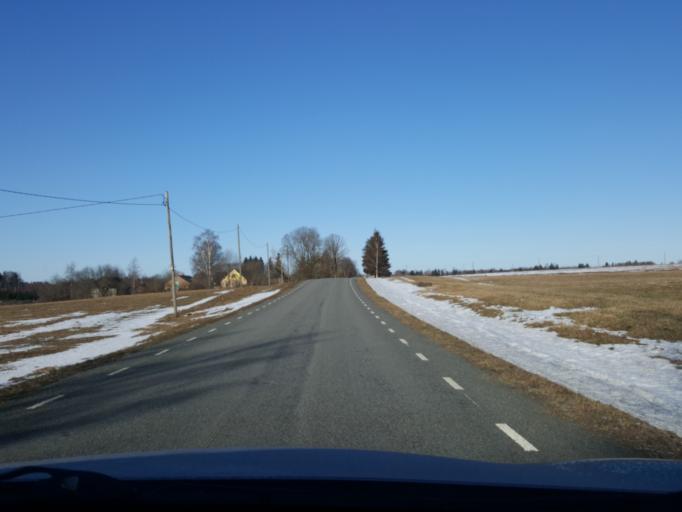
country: EE
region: Viljandimaa
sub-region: Viljandi linn
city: Viljandi
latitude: 58.4104
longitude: 25.5594
